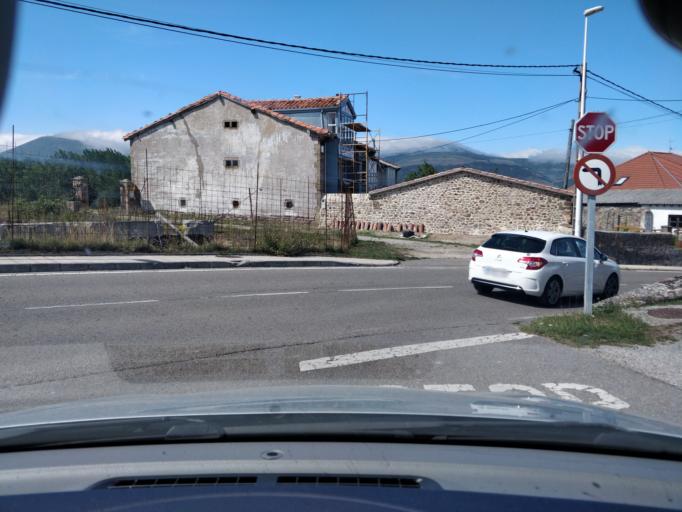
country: ES
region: Cantabria
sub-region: Provincia de Cantabria
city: Reinosa
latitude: 42.9984
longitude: -4.1560
